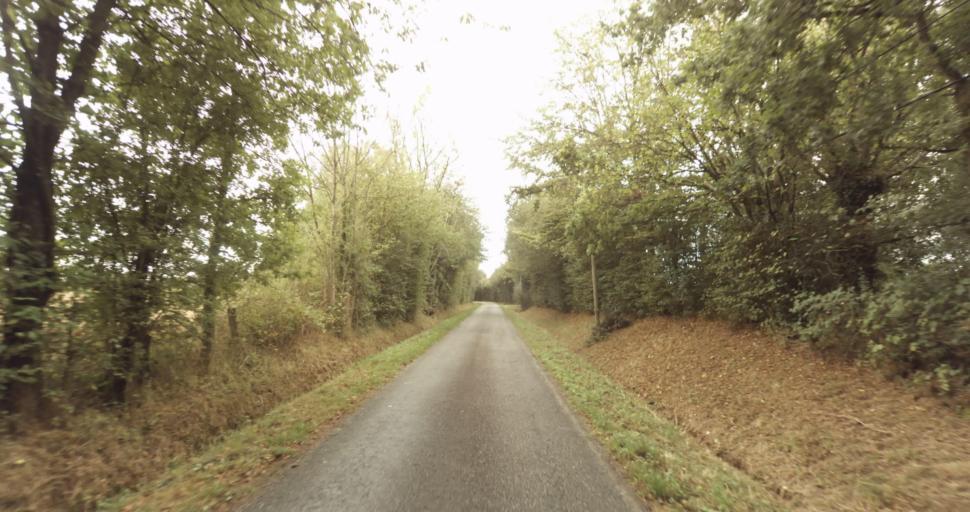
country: FR
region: Lower Normandy
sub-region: Departement de l'Orne
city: Sainte-Gauburge-Sainte-Colombe
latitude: 48.7155
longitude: 0.4601
